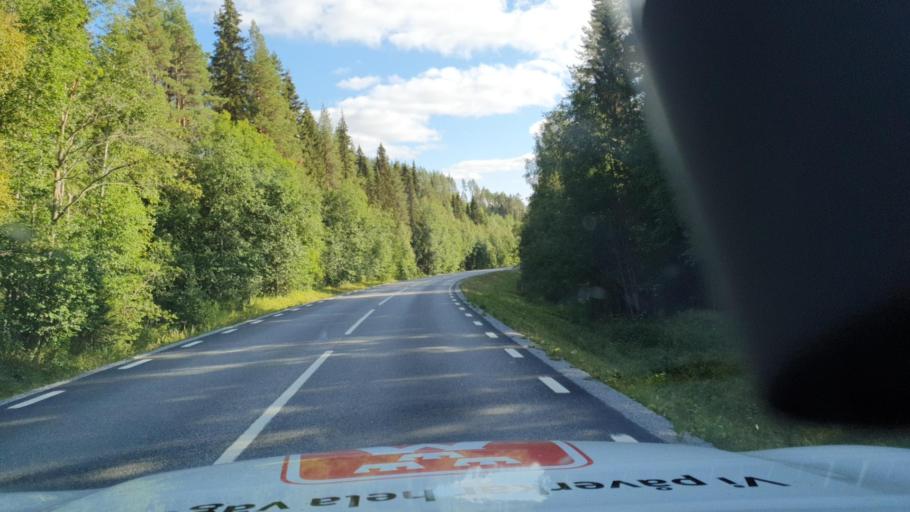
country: SE
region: Vaesterbotten
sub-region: Dorotea Kommun
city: Dorotea
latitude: 63.8659
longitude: 16.3841
